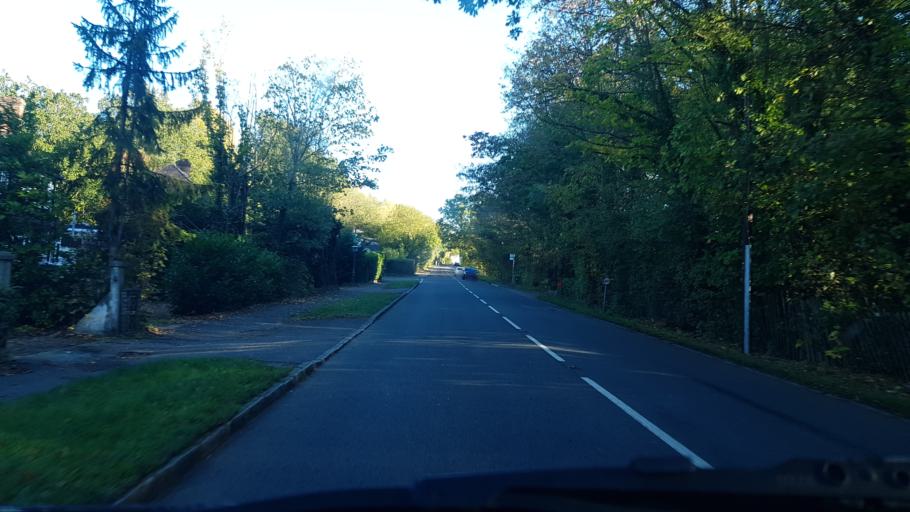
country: GB
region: England
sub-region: Surrey
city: Guildford
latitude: 51.2563
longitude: -0.6079
